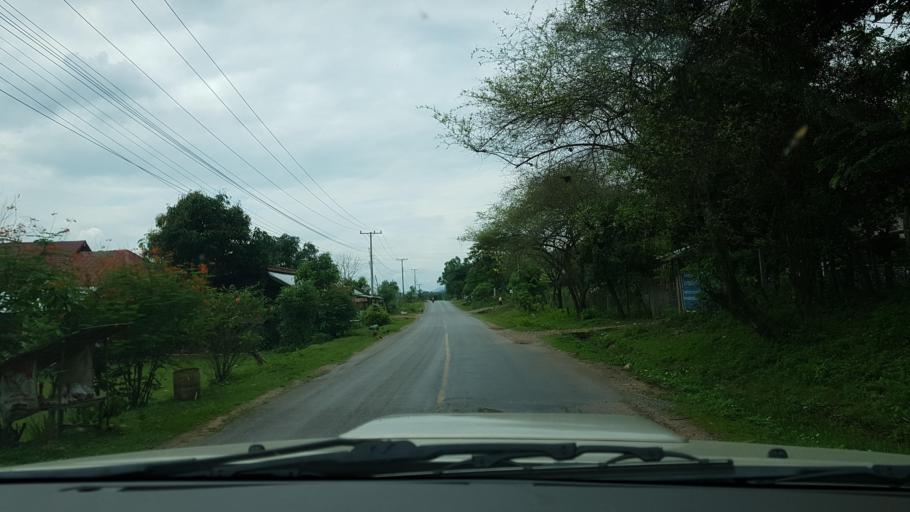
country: LA
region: Loungnamtha
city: Muang Nale
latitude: 20.3490
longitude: 101.6828
